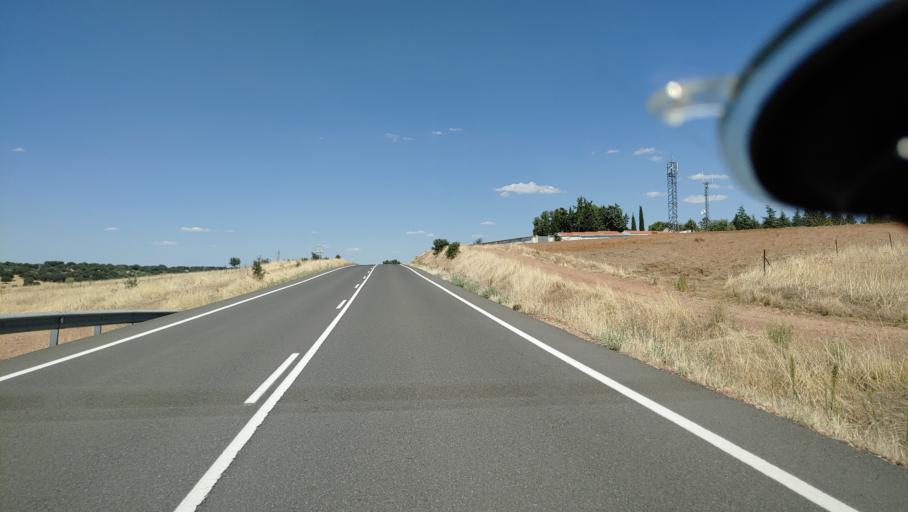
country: ES
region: Castille-La Mancha
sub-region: Provincia de Ciudad Real
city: Saceruela
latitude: 38.9457
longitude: -4.6132
